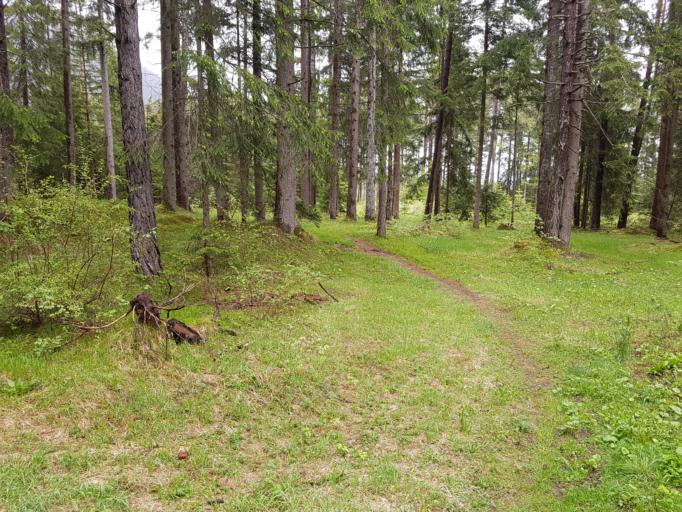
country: AT
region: Tyrol
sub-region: Politischer Bezirk Imst
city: Obsteig
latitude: 47.3014
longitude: 10.9075
